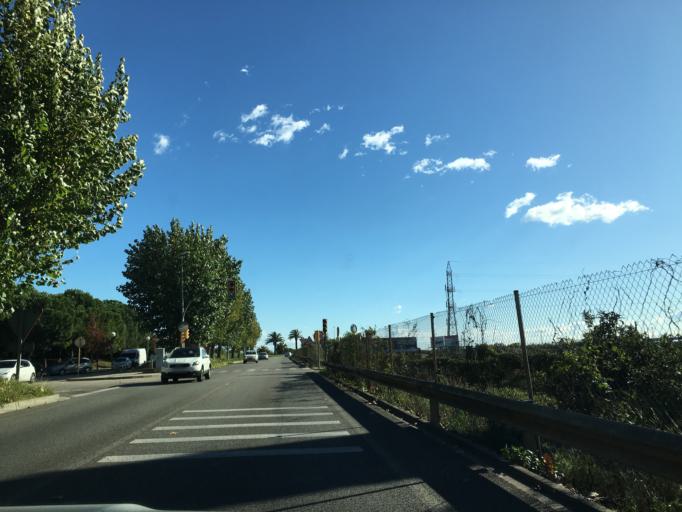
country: ES
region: Catalonia
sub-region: Provincia de Barcelona
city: Sant Joan Despi
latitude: 41.3630
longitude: 2.0542
